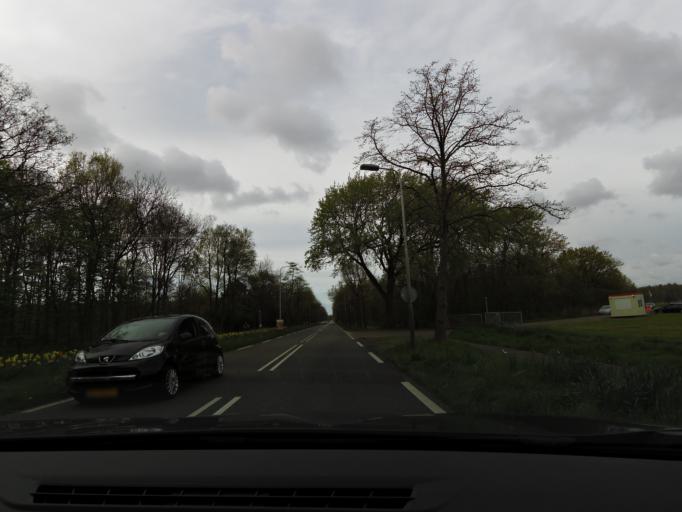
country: NL
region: South Holland
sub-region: Gemeente Lisse
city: Lisse
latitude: 52.2713
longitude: 4.5398
